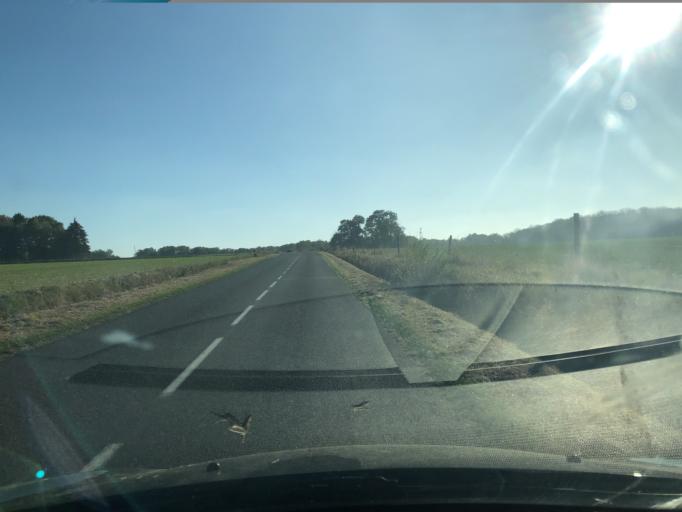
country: FR
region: Centre
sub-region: Departement d'Indre-et-Loire
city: Neuvy-le-Roi
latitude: 47.5945
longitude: 0.5957
